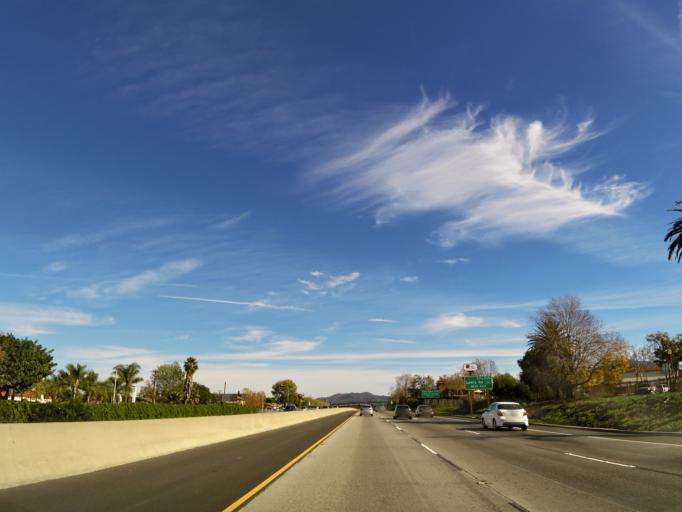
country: US
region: California
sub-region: Ventura County
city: Camarillo
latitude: 34.2174
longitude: -119.0450
